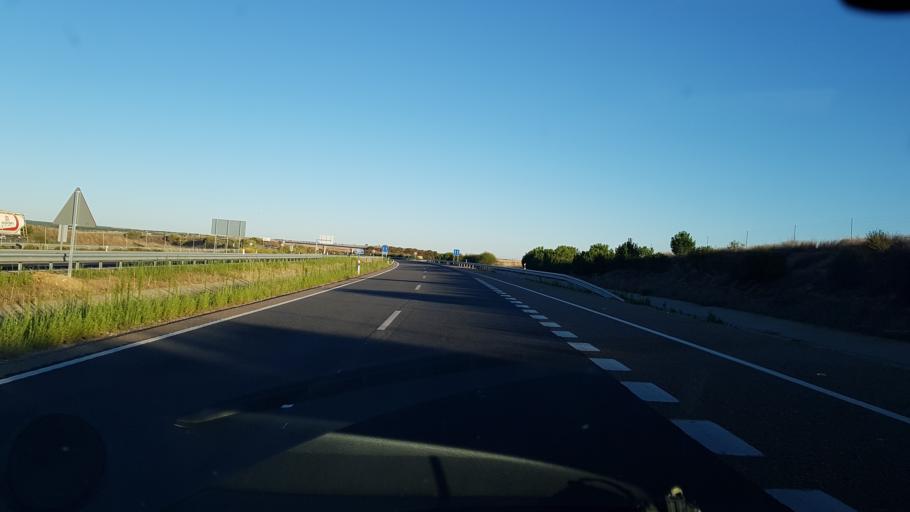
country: ES
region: Castille and Leon
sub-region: Provincia de Zamora
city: Toro
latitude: 41.5468
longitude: -5.3824
